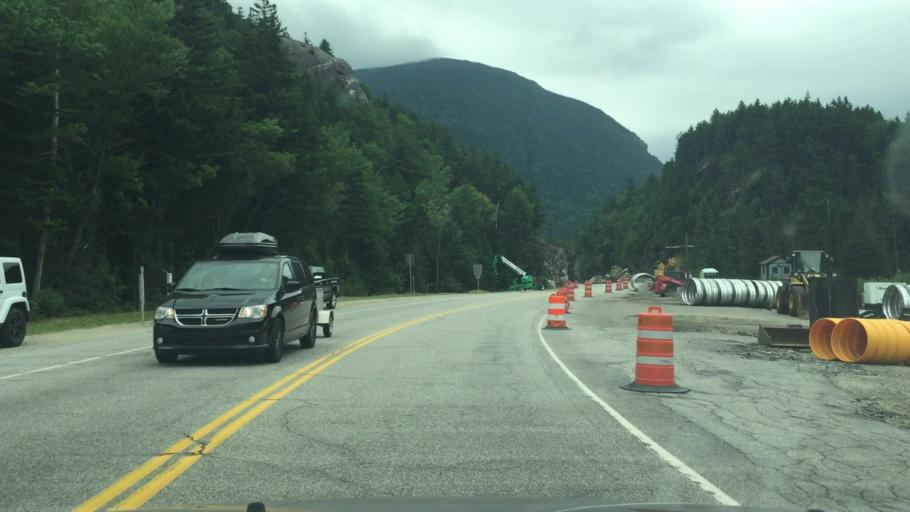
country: US
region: New Hampshire
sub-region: Grafton County
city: Deerfield
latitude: 44.2148
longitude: -71.4078
